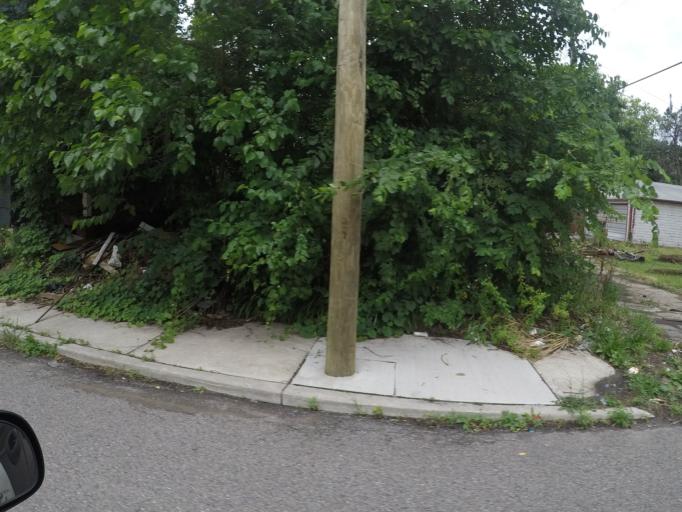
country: US
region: Michigan
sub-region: Wayne County
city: Detroit
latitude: 42.3585
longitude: -83.0066
